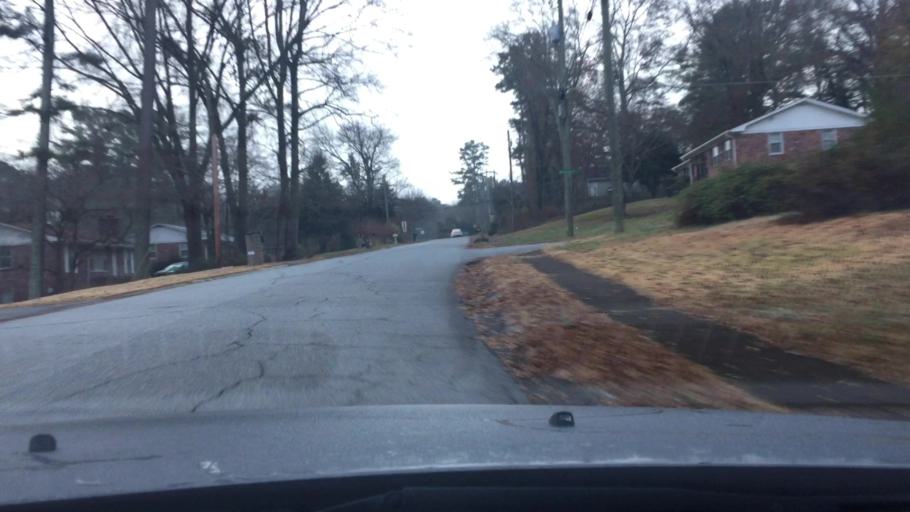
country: US
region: Georgia
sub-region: Cobb County
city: Marietta
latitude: 34.0154
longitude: -84.5433
